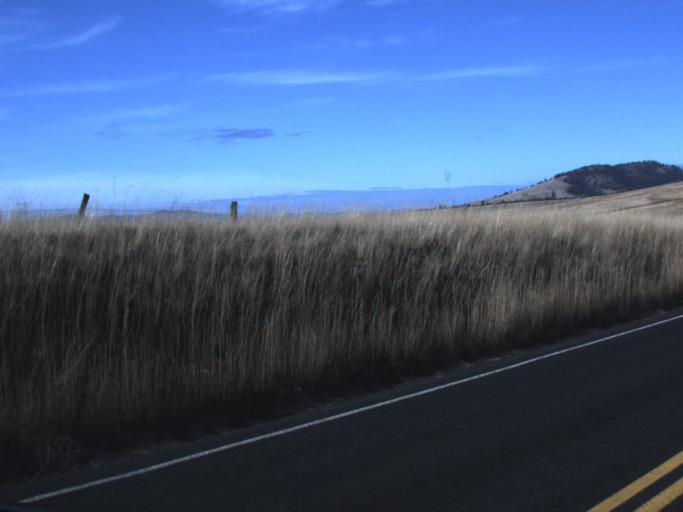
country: US
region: Washington
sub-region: Lincoln County
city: Davenport
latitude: 47.8560
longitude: -118.2143
